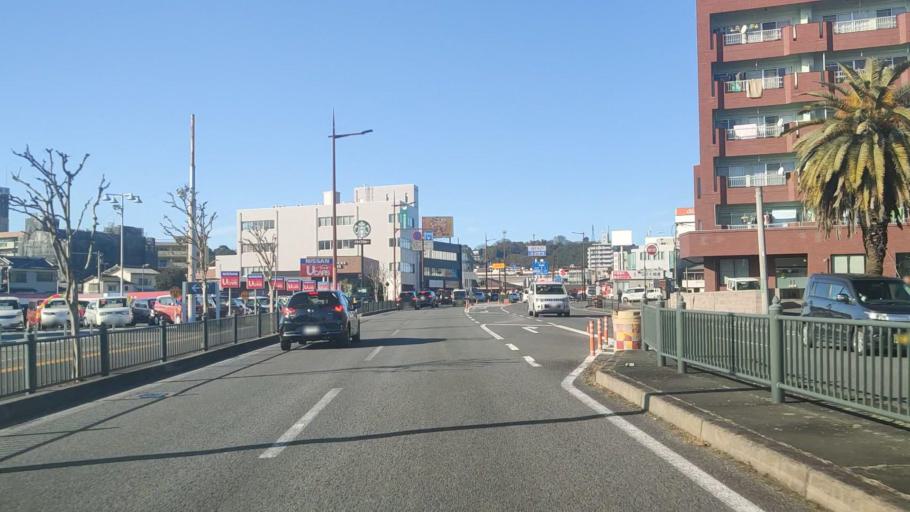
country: JP
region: Oita
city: Oita
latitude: 33.2118
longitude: 131.5974
